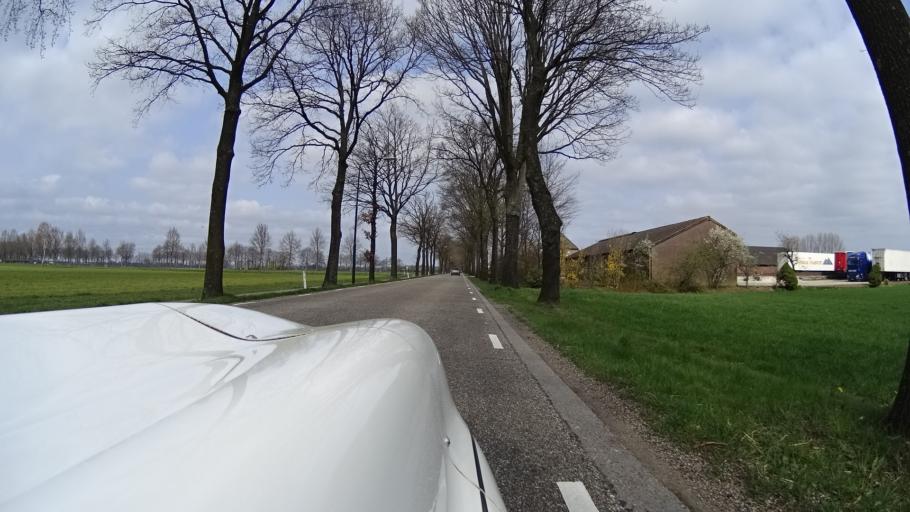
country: NL
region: North Brabant
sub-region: Gemeente Veghel
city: Zijtaart
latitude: 51.5643
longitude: 5.5561
